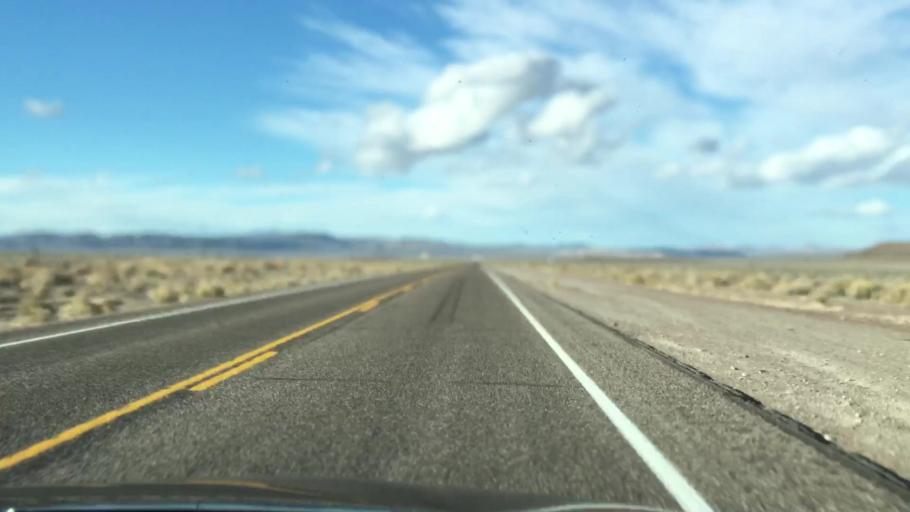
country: US
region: Nevada
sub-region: Esmeralda County
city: Goldfield
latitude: 37.3908
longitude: -117.1449
